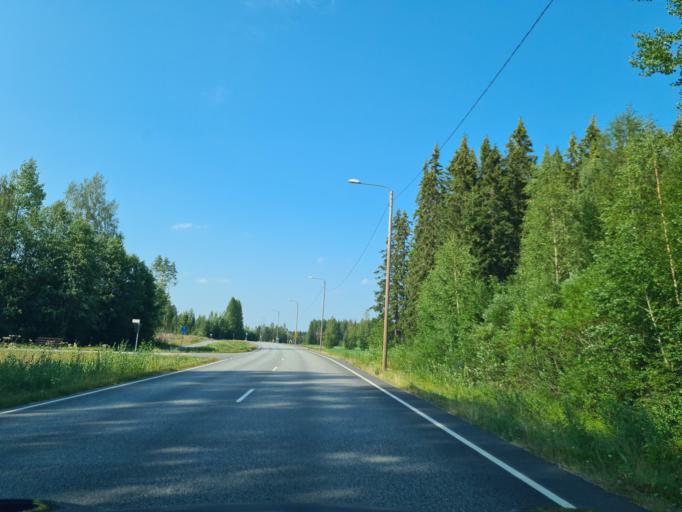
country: FI
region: Satakunta
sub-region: Pohjois-Satakunta
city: Karvia
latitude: 62.0861
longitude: 22.5270
